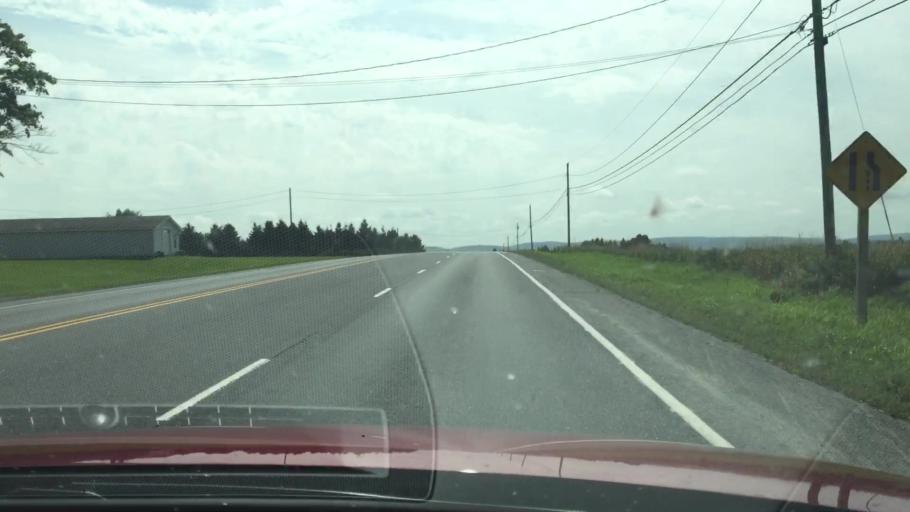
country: US
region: Maine
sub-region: Aroostook County
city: Easton
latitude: 46.5777
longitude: -67.9555
